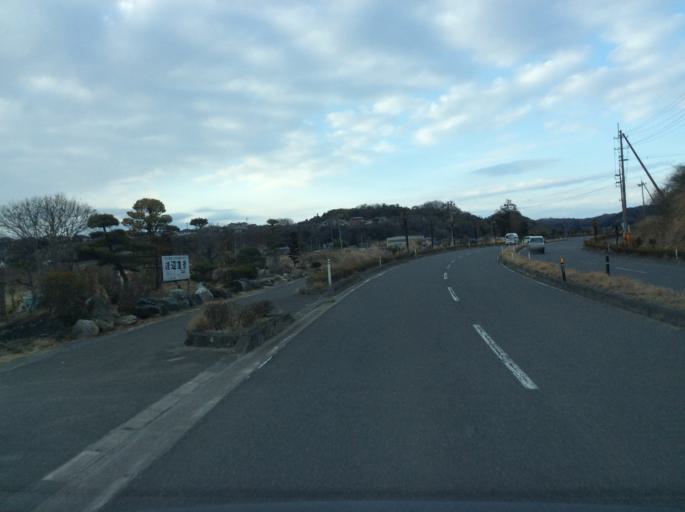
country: JP
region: Fukushima
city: Iwaki
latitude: 36.9557
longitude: 140.9191
